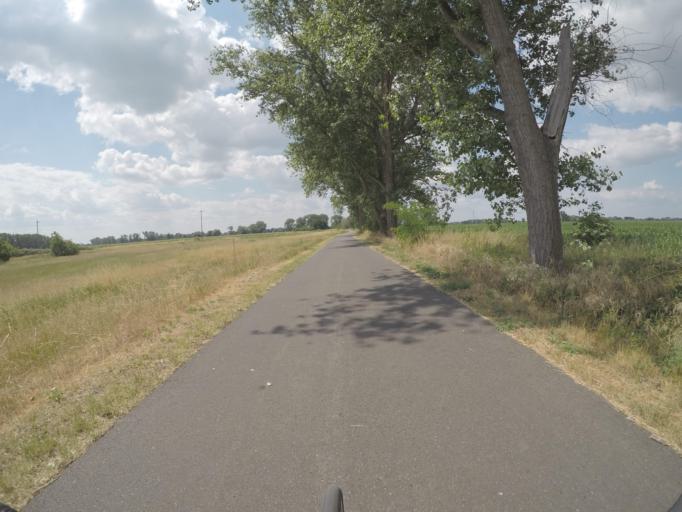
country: DE
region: Brandenburg
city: Roskow
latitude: 52.4717
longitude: 12.7060
